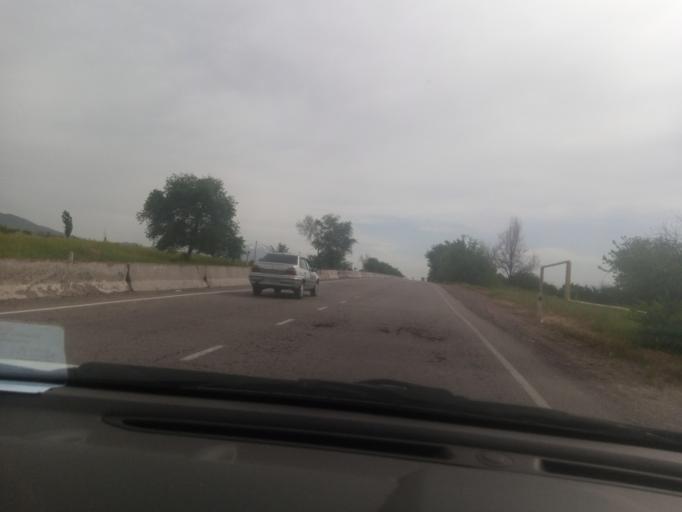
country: UZ
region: Toshkent
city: Angren
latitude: 40.9552
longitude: 69.9287
